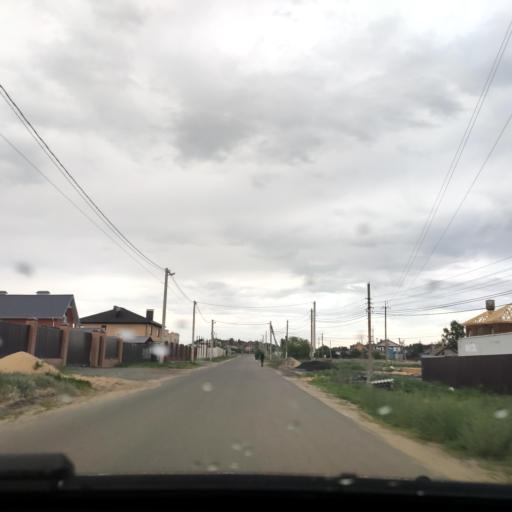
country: RU
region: Voronezj
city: Podgornoye
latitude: 51.7715
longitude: 39.1232
